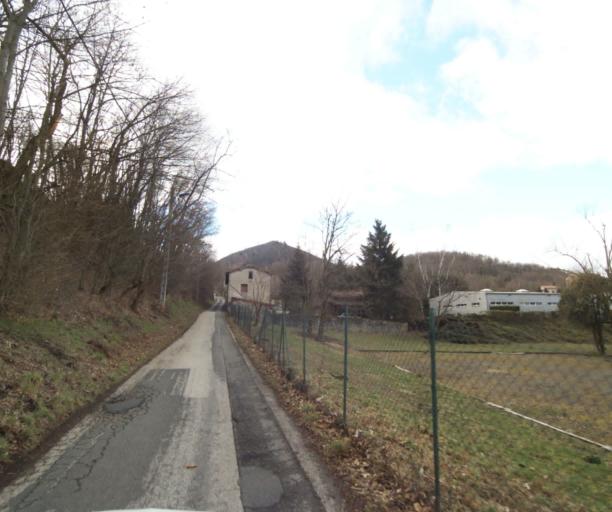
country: FR
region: Rhone-Alpes
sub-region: Departement de la Loire
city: La Talaudiere
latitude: 45.4716
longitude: 4.4400
